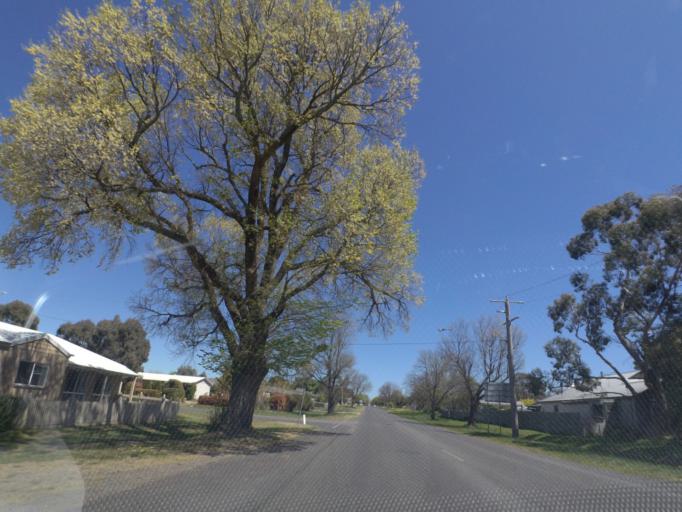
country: AU
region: Victoria
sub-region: Hume
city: Sunbury
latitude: -37.2792
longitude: 144.7358
